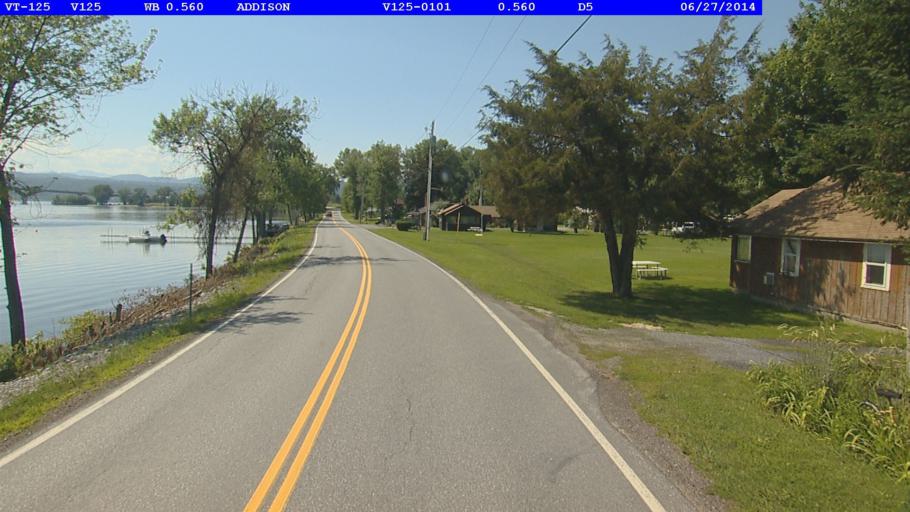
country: US
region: New York
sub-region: Essex County
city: Port Henry
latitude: 44.0324
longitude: -73.4087
